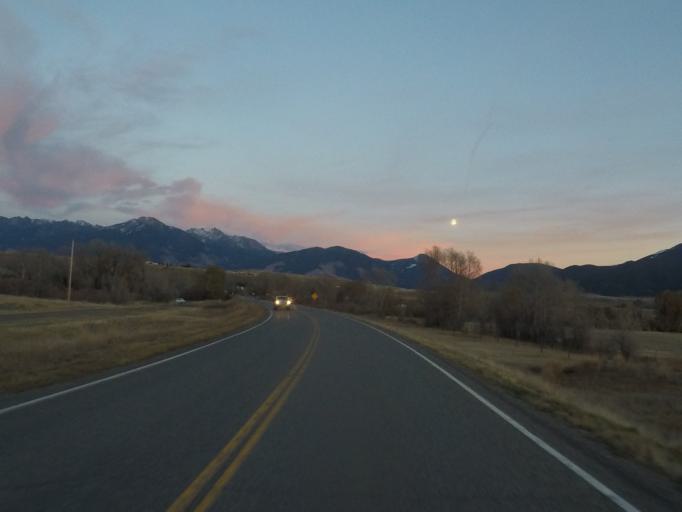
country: US
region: Montana
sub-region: Park County
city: Livingston
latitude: 45.3677
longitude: -110.7306
